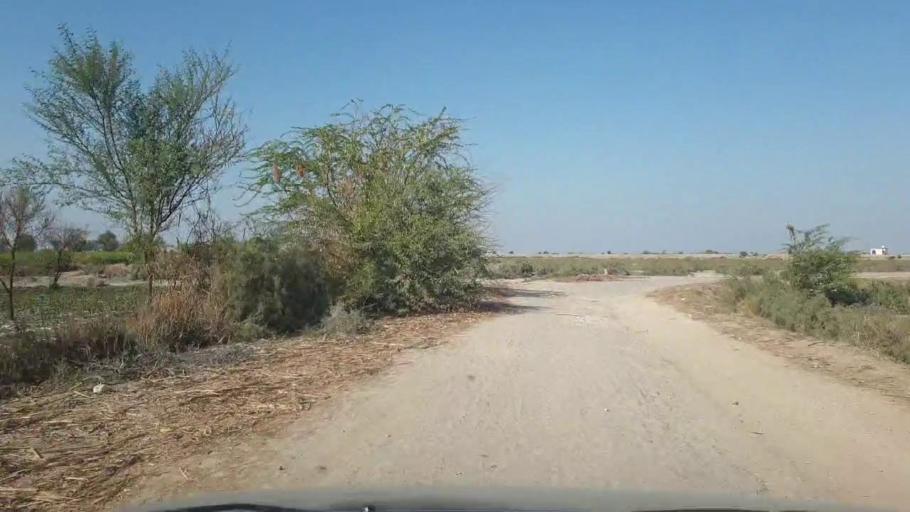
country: PK
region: Sindh
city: Samaro
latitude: 25.3729
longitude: 69.3276
